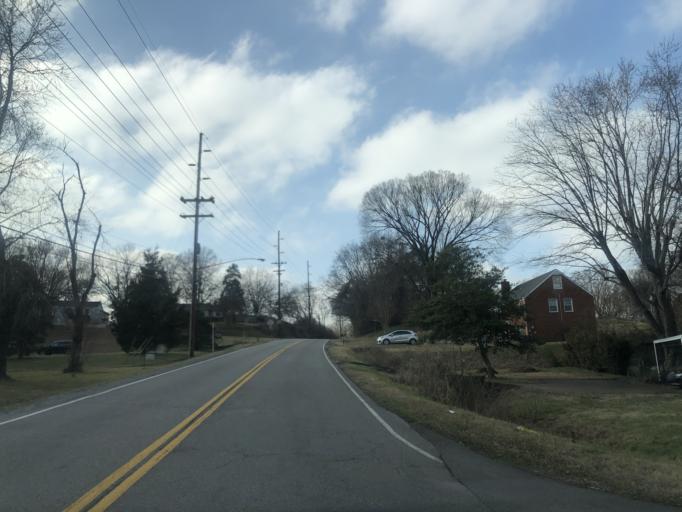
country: US
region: Tennessee
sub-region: Davidson County
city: Oak Hill
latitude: 36.0984
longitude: -86.7205
